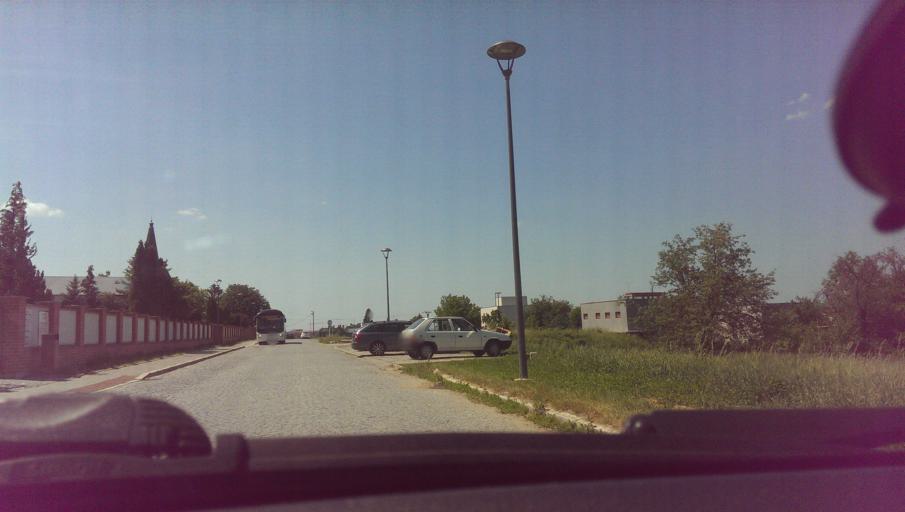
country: CZ
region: Zlin
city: Kunovice
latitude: 49.0647
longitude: 17.4881
